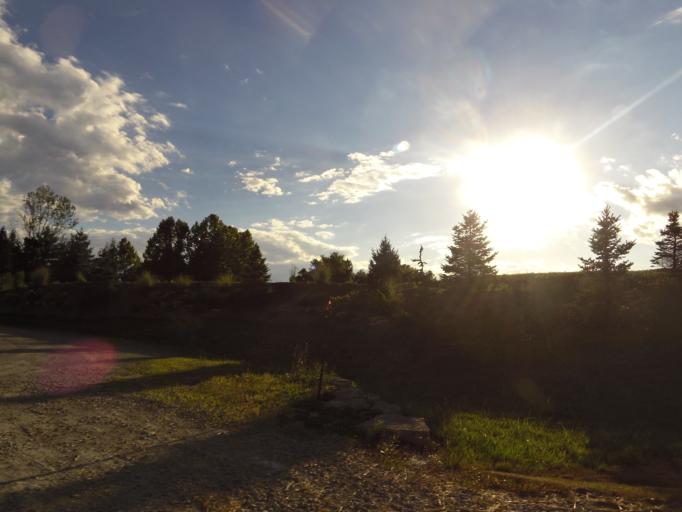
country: US
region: Missouri
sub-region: Saint Louis County
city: Wildwood
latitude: 38.6331
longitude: -90.6616
